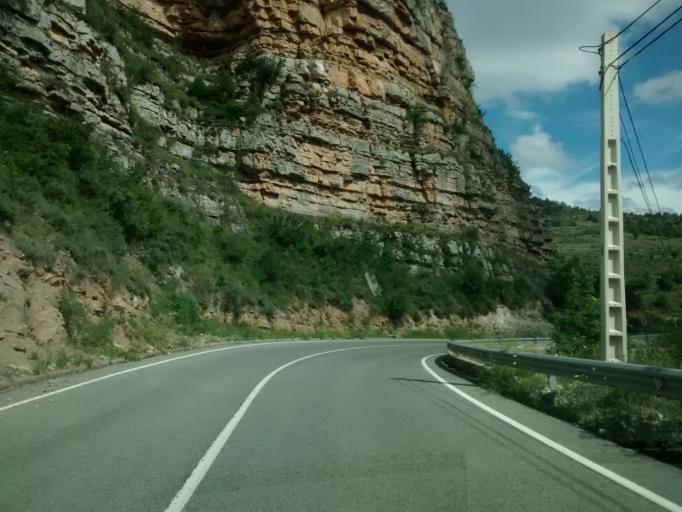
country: ES
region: La Rioja
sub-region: Provincia de La Rioja
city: Soto en Cameros
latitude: 42.3015
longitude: -2.4191
